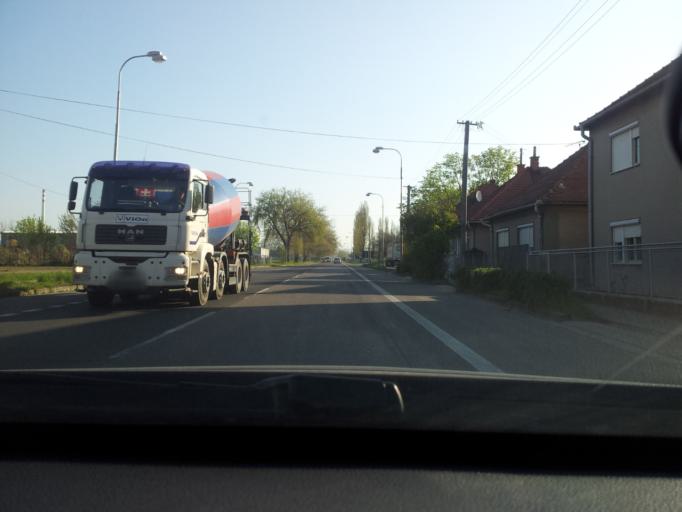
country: SK
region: Nitriansky
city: Zlate Moravce
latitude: 48.3894
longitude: 18.3927
